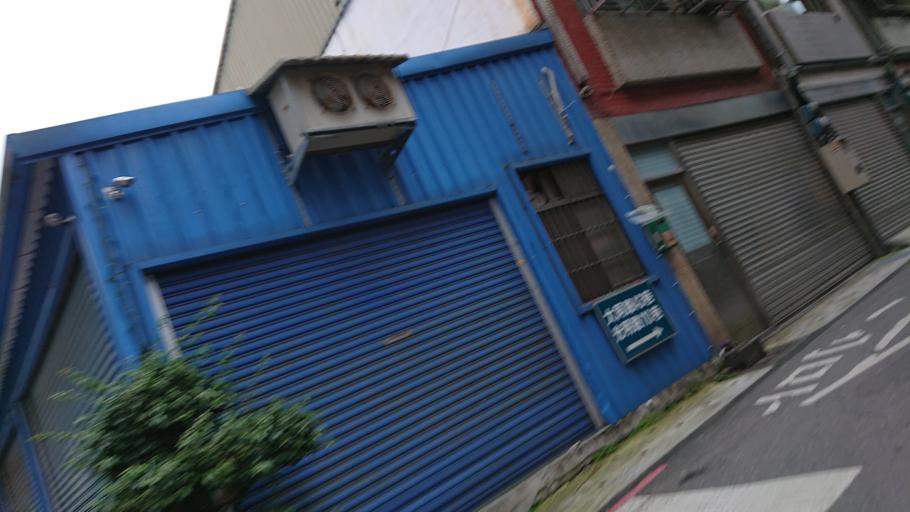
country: TW
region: Taiwan
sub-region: Taoyuan
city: Taoyuan
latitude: 24.9276
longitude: 121.3766
